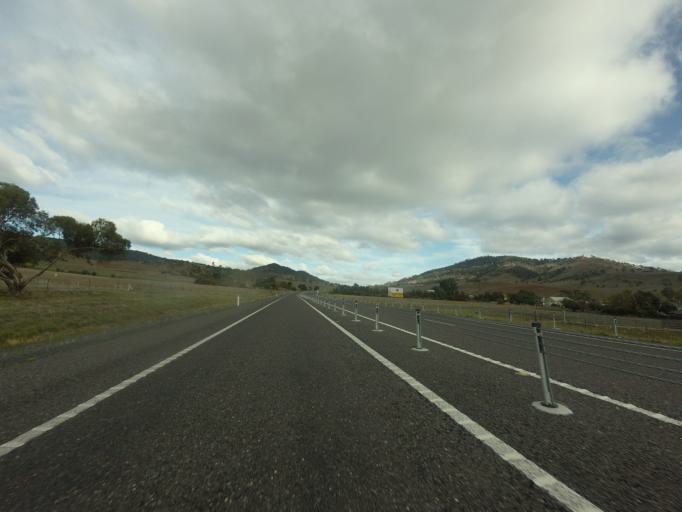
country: AU
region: Tasmania
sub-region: Brighton
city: Bridgewater
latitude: -42.5340
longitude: 147.2051
